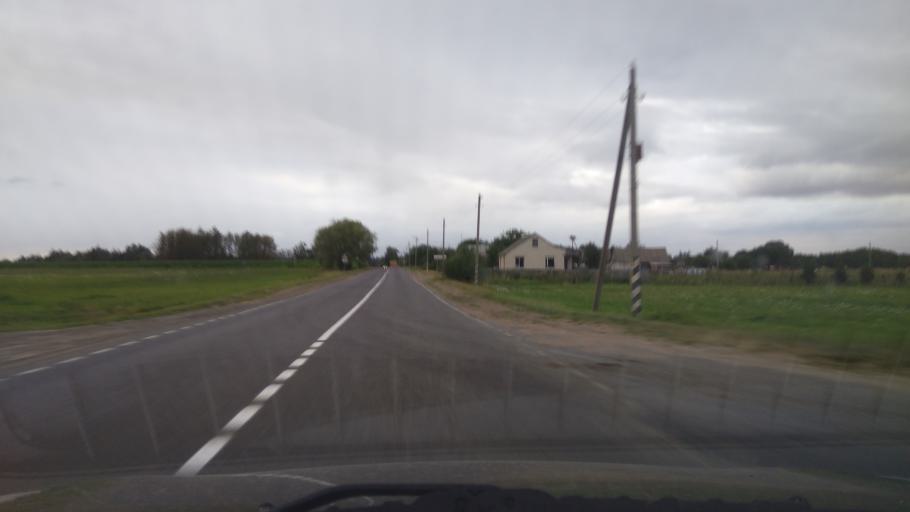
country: BY
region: Brest
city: Byaroza
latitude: 52.4519
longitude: 24.9700
